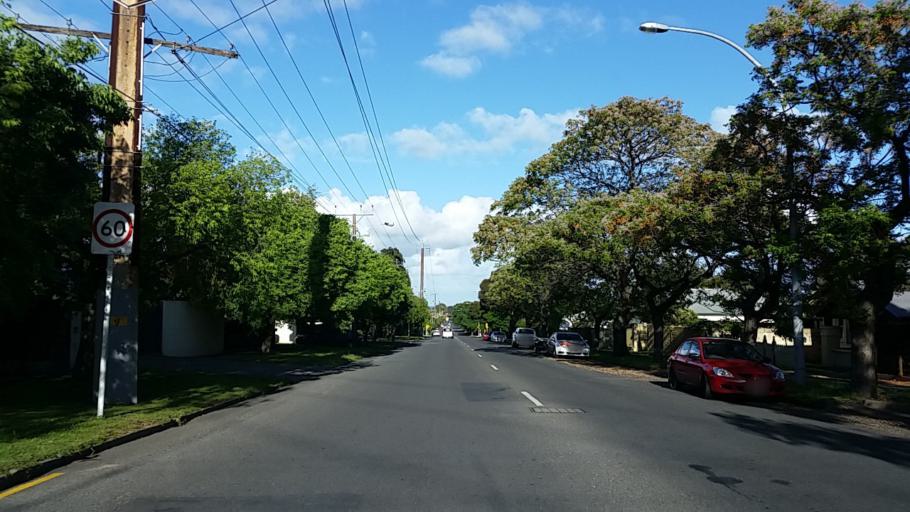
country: AU
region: South Australia
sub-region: Mitcham
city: Clapham
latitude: -34.9904
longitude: 138.6015
